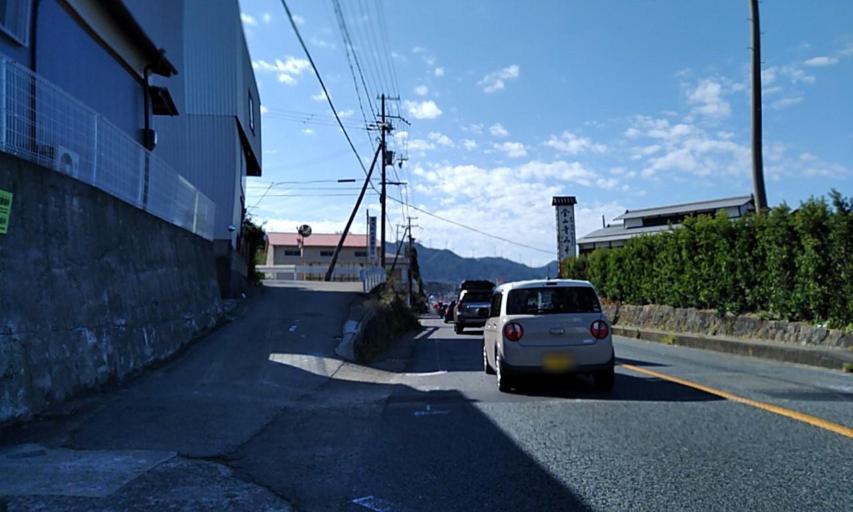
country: JP
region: Wakayama
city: Kainan
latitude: 34.0285
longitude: 135.1833
